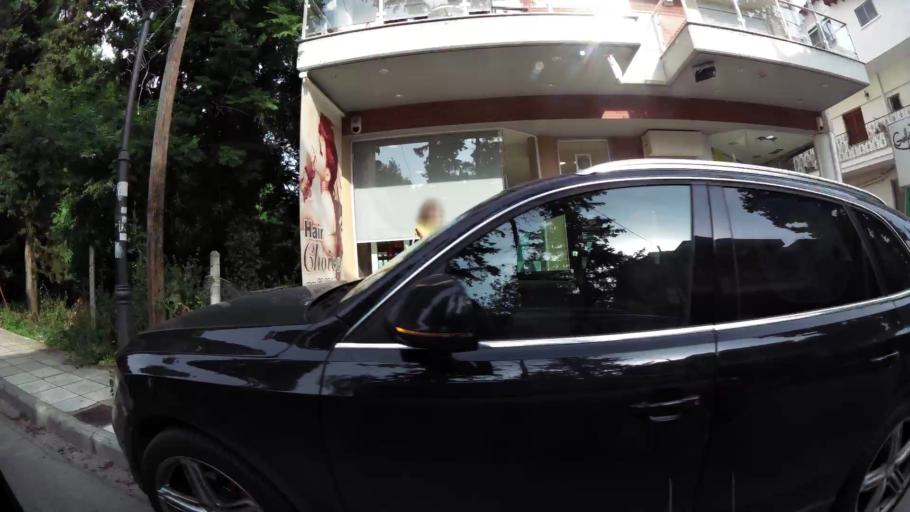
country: GR
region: Central Macedonia
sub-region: Nomos Thessalonikis
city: Oraiokastro
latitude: 40.7322
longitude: 22.9182
